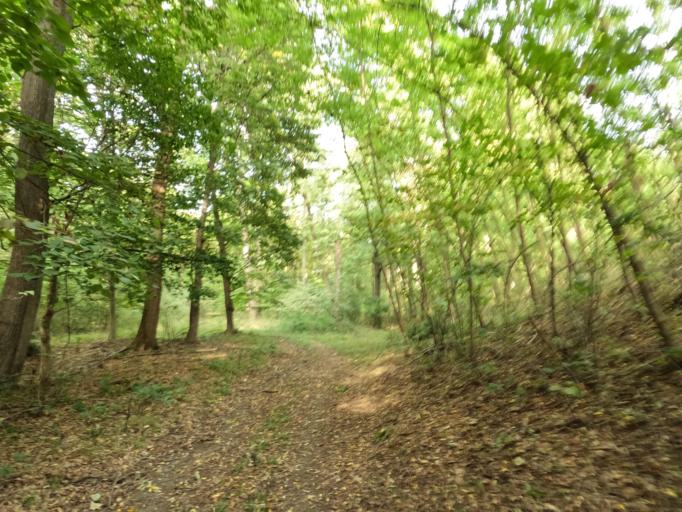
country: HU
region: Tolna
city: Szekszard
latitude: 46.3168
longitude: 18.6640
